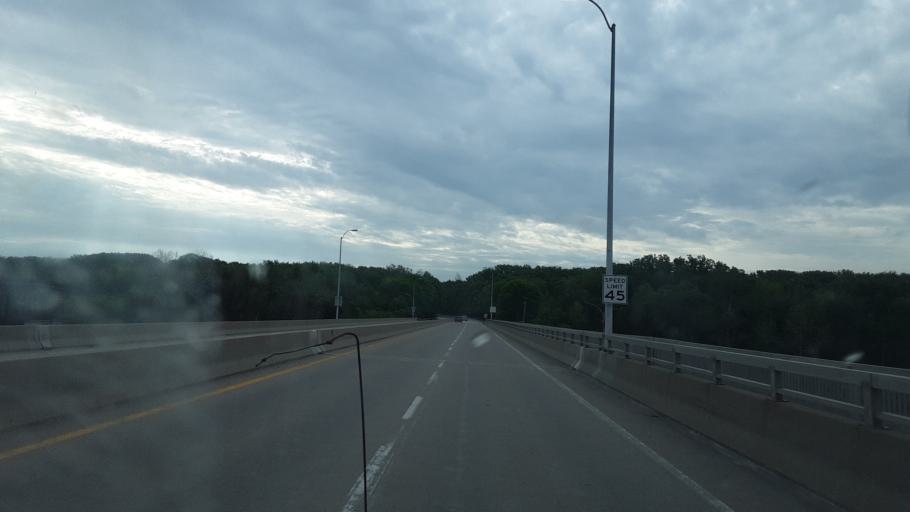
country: US
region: Iowa
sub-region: Lee County
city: Keokuk
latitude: 40.3898
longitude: -91.3719
